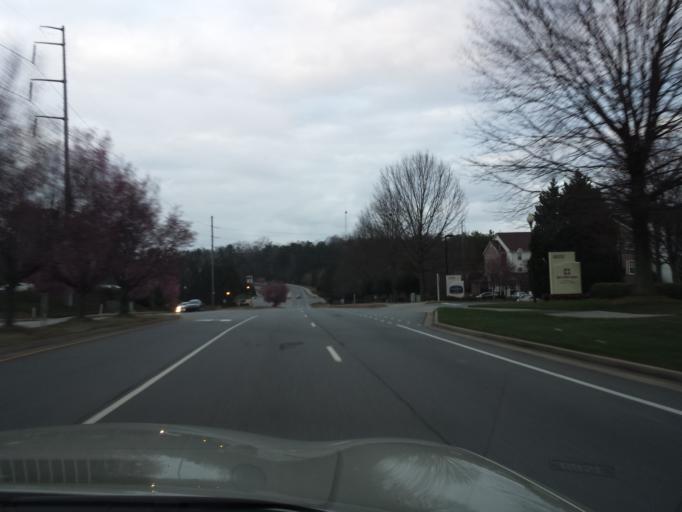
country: US
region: Georgia
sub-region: Fulton County
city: Alpharetta
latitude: 34.0611
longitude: -84.2878
